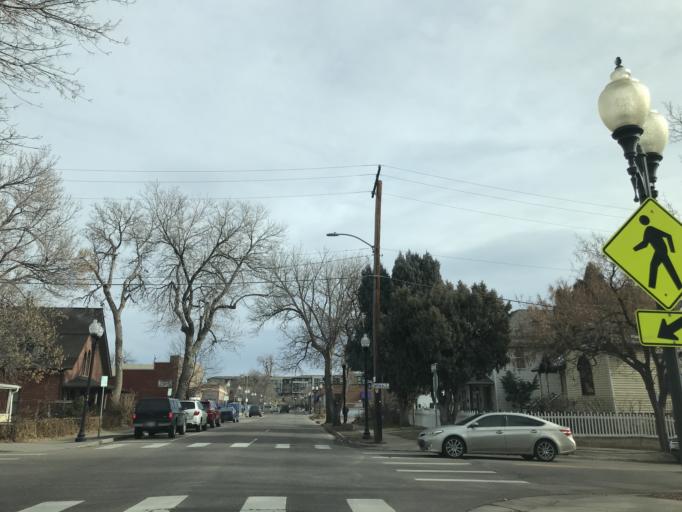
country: US
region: Colorado
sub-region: Arapahoe County
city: Littleton
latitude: 39.6128
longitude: -105.0186
